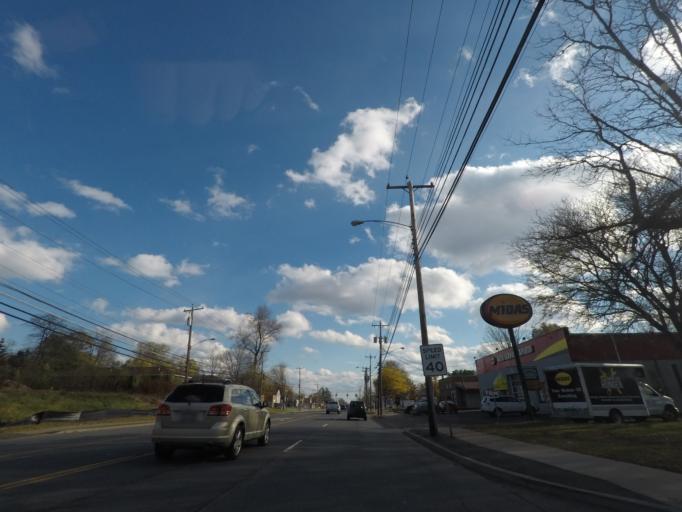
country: US
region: New York
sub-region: Albany County
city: Colonie
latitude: 42.7254
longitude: -73.8418
